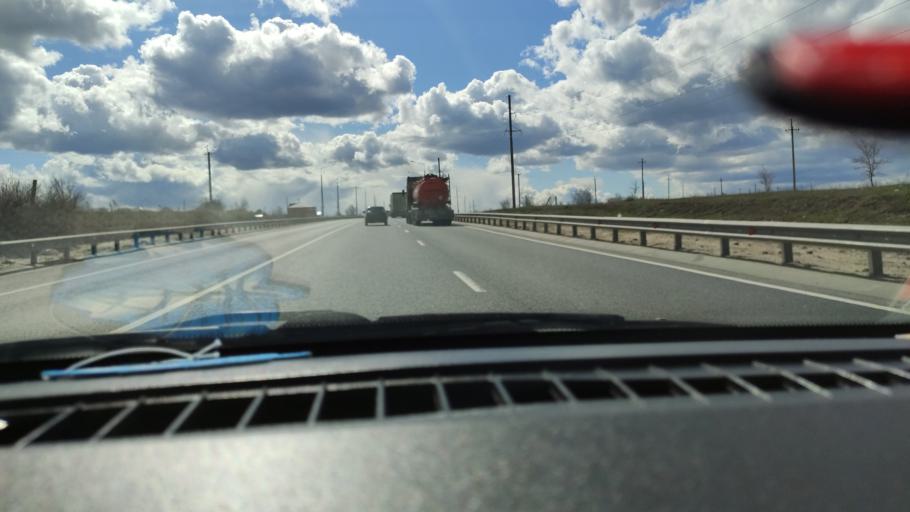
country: RU
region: Samara
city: Varlamovo
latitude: 53.1973
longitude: 48.3710
